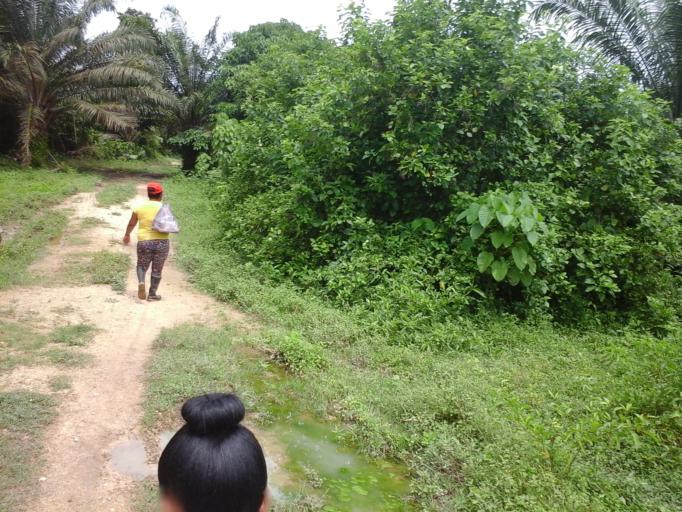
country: CO
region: Bolivar
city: San Pablo
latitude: 10.1617
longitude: -75.2758
